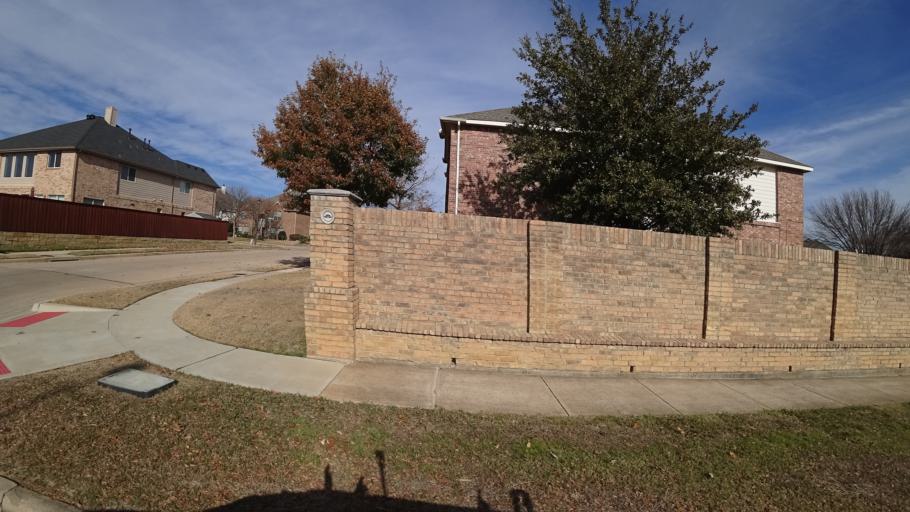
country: US
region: Texas
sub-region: Denton County
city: Highland Village
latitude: 33.0626
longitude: -97.0323
